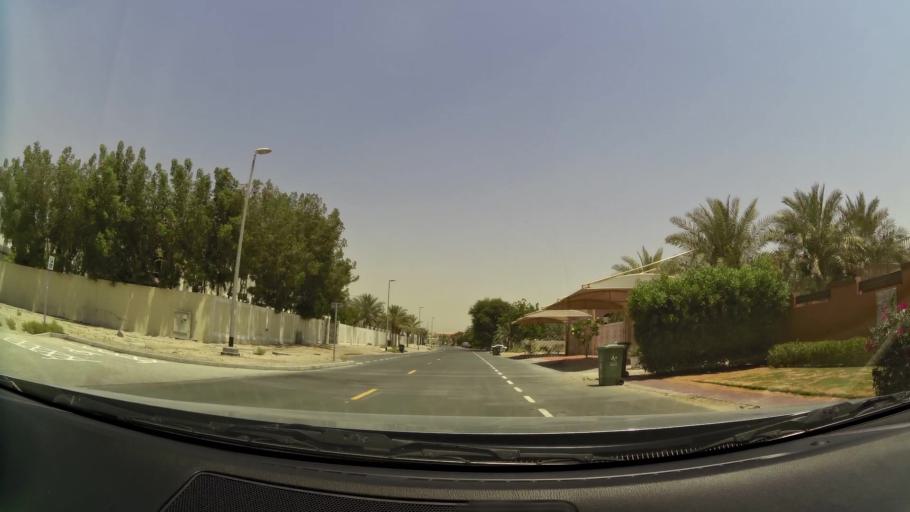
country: AE
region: Dubai
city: Dubai
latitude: 25.0862
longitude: 55.2001
